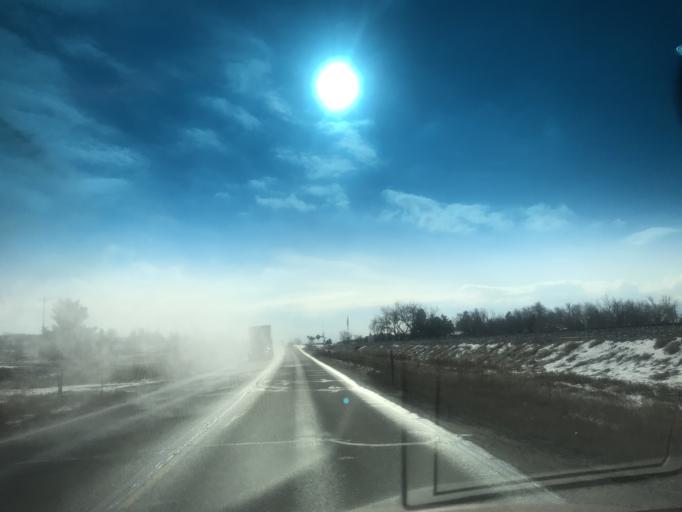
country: US
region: Colorado
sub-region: Douglas County
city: Highlands Ranch
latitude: 39.4839
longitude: -104.9948
